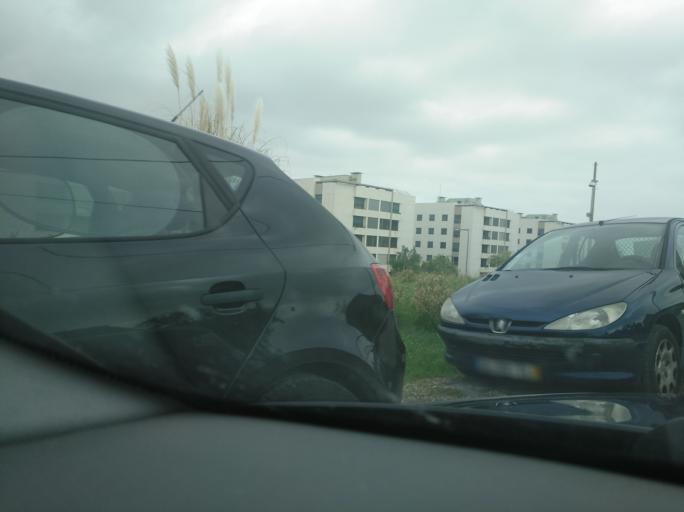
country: PT
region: Lisbon
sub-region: Odivelas
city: Pontinha
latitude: 38.7470
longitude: -9.1771
